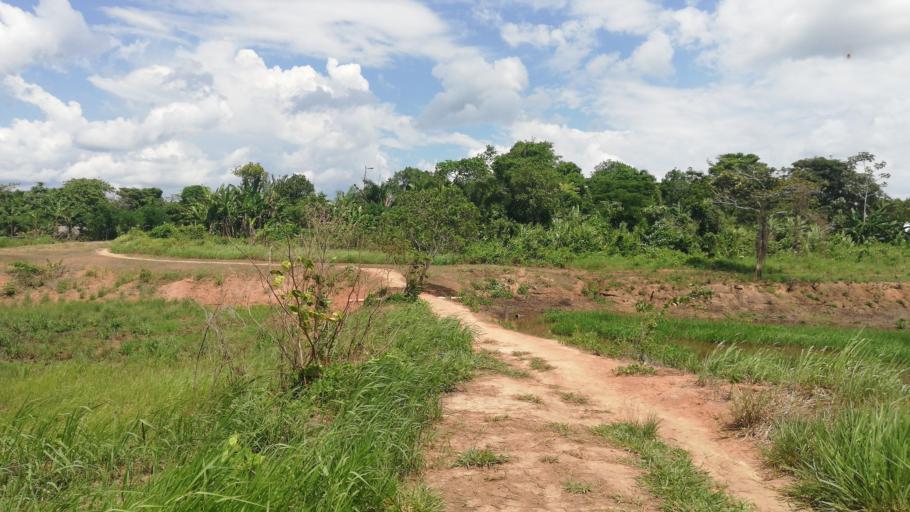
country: PE
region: Ucayali
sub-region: Provincia de Coronel Portillo
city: Puerto Callao
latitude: -8.2704
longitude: -74.6516
